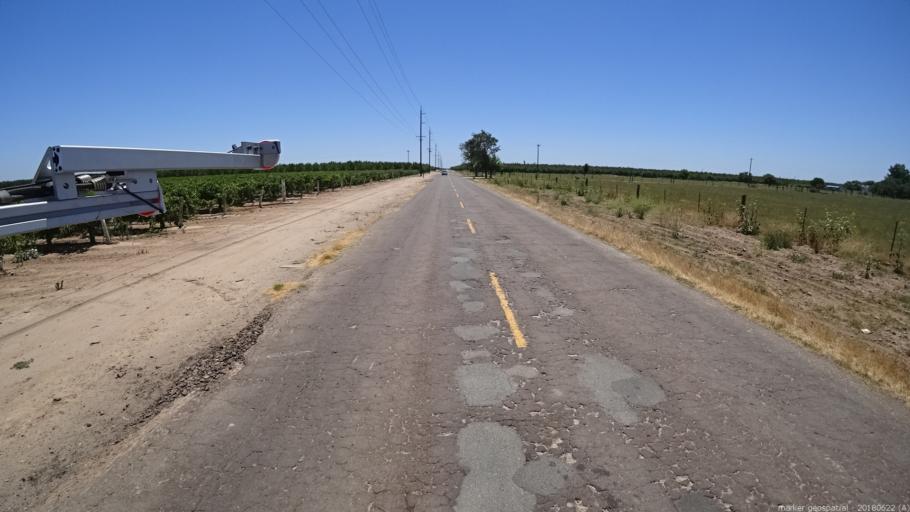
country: US
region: California
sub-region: Madera County
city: Parksdale
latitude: 36.9155
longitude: -119.9923
